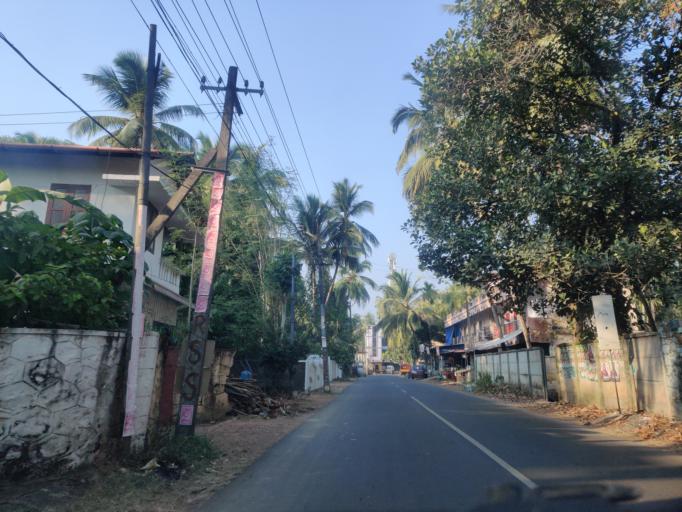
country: IN
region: Kerala
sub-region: Malappuram
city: Ponnani
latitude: 10.7324
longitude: 76.0126
